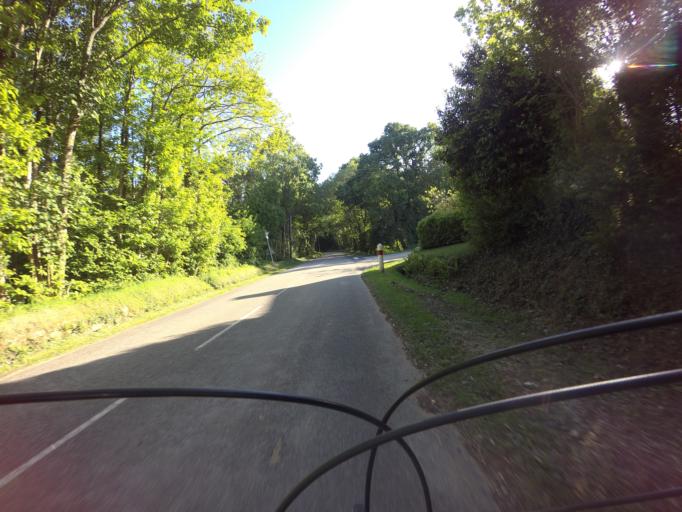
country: FR
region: Brittany
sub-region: Departement du Finistere
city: Quimper
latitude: 48.0193
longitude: -4.1345
